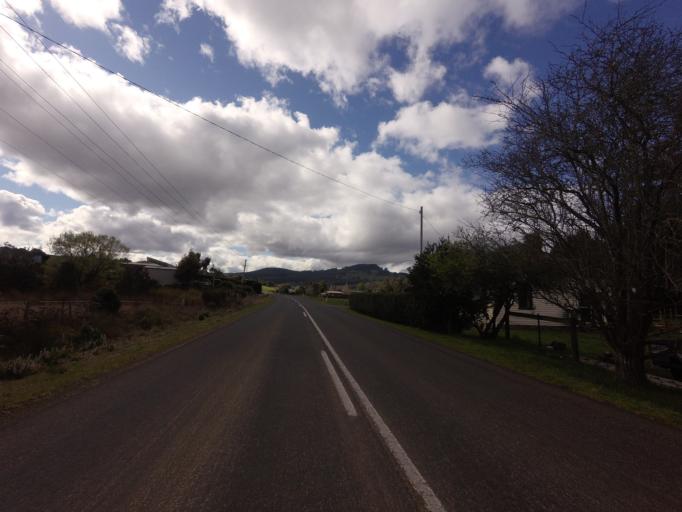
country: AU
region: Tasmania
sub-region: Huon Valley
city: Geeveston
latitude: -43.1747
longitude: 146.9238
